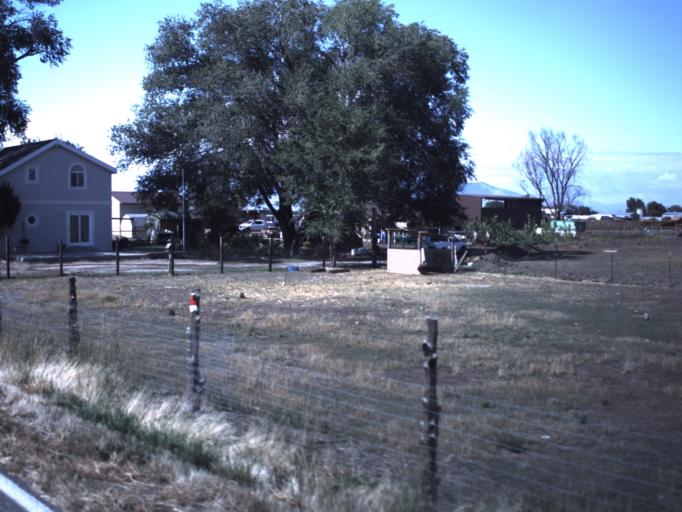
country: US
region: Utah
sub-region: Utah County
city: Benjamin
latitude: 40.1147
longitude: -111.7256
